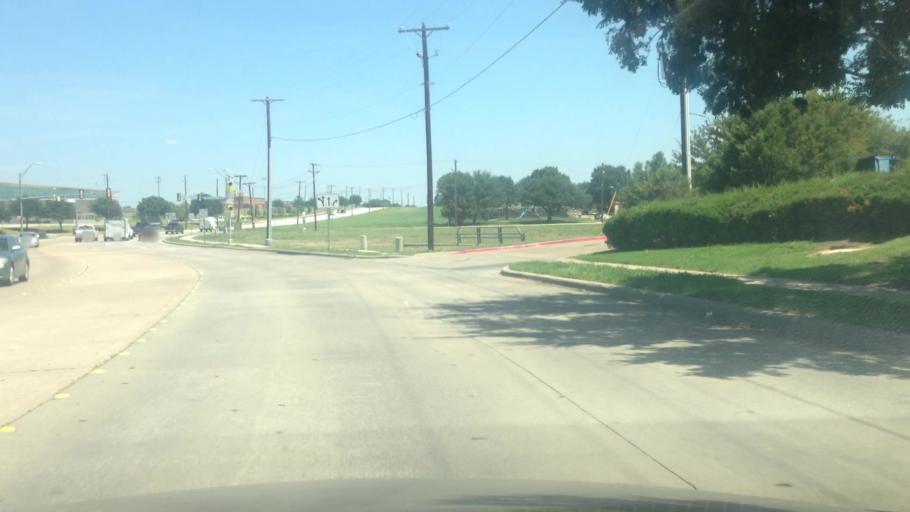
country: US
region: Texas
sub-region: Tarrant County
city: Watauga
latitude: 32.8921
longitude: -97.2565
